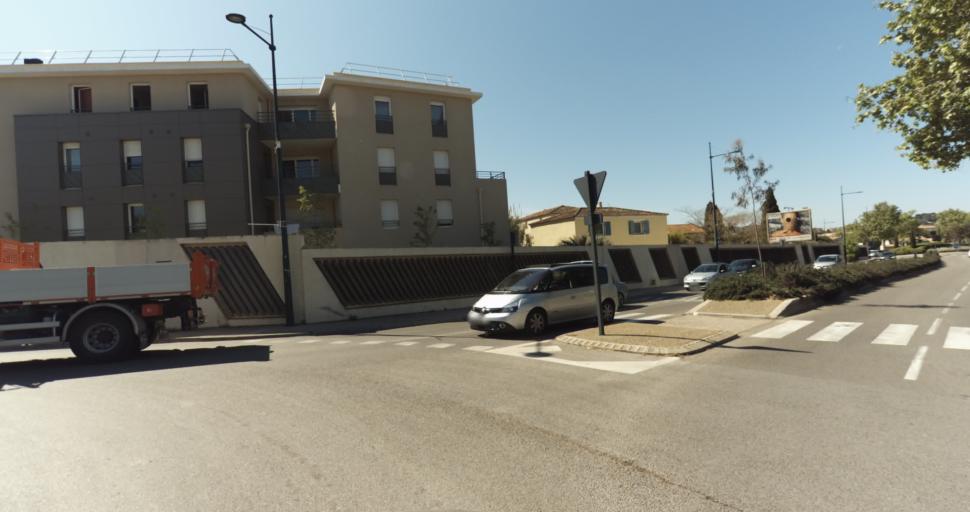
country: FR
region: Provence-Alpes-Cote d'Azur
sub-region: Departement du Var
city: Six-Fours-les-Plages
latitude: 43.0955
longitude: 5.8481
